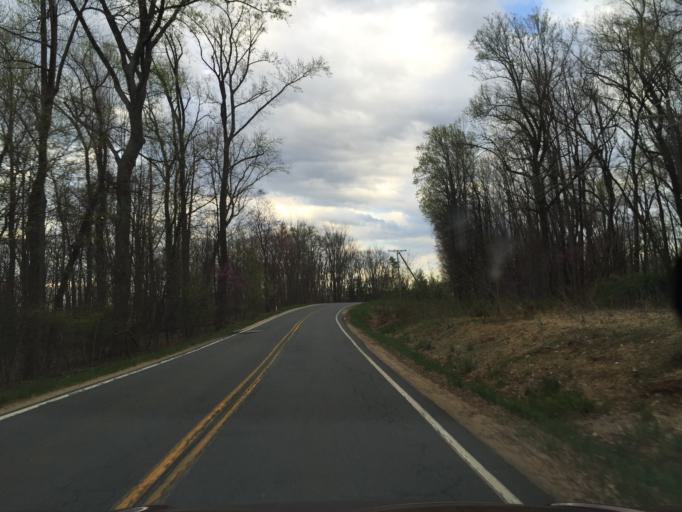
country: US
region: Maryland
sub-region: Frederick County
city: Point of Rocks
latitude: 39.2444
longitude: -77.5590
